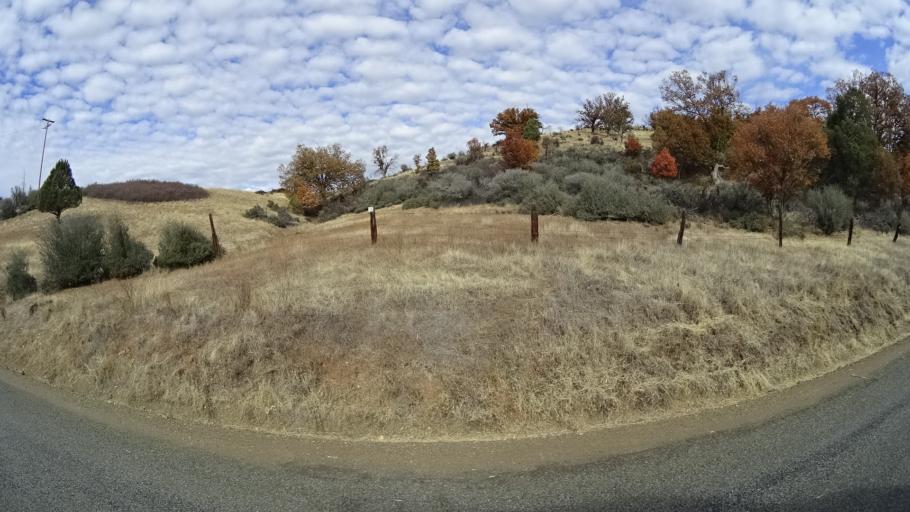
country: US
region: California
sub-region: Siskiyou County
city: Yreka
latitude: 41.6261
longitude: -122.7781
